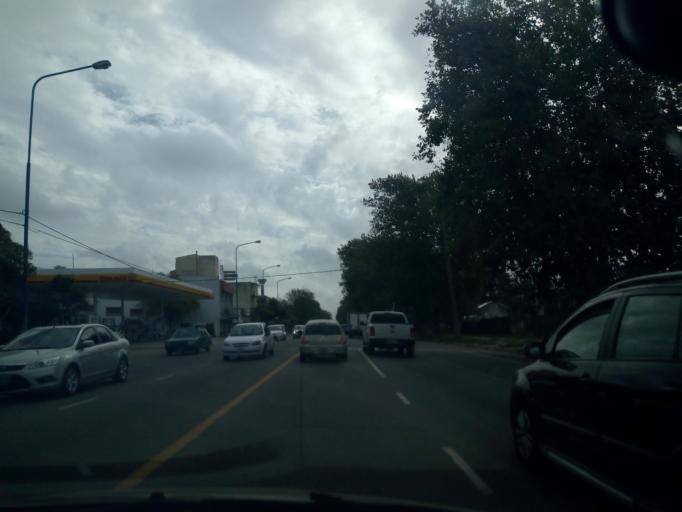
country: AR
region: Buenos Aires
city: Mar del Plata
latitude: -37.9881
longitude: -57.5669
